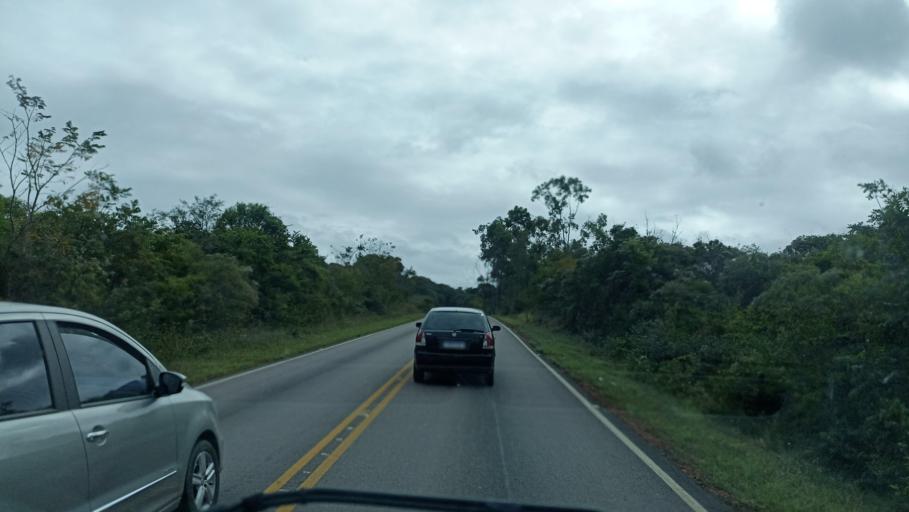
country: BR
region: Bahia
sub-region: Andarai
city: Vera Cruz
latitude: -12.9301
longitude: -41.2466
